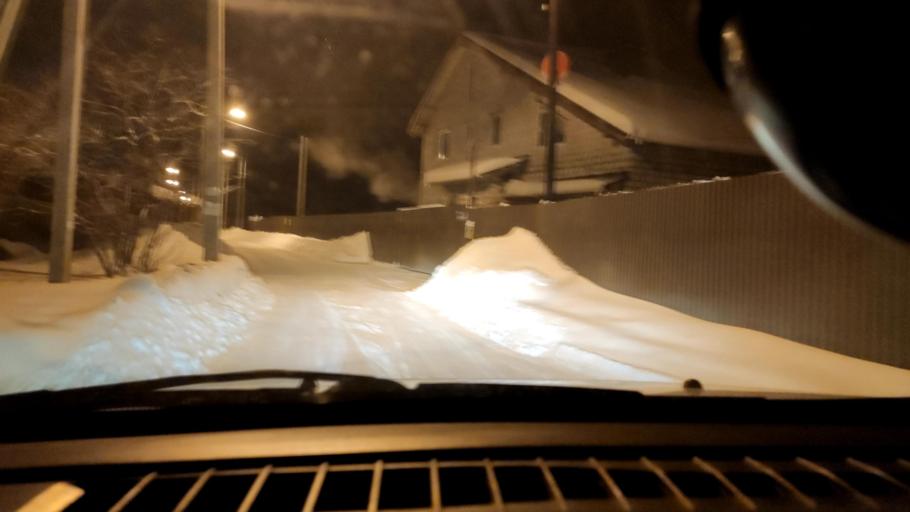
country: RU
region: Perm
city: Kondratovo
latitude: 58.0261
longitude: 55.9921
